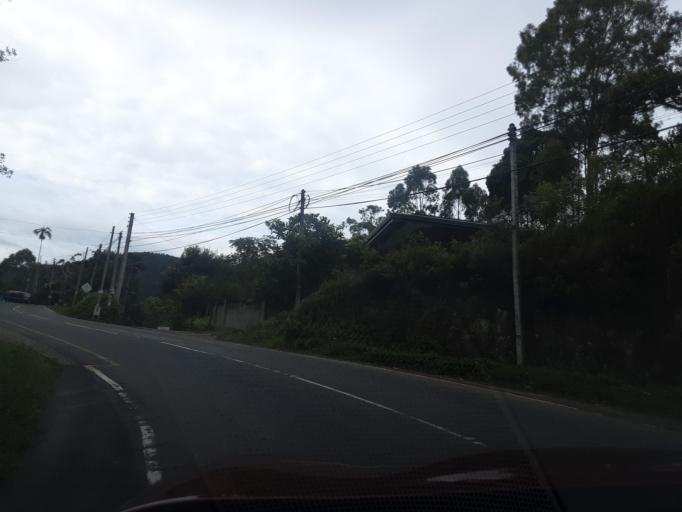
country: LK
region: Uva
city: Haputale
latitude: 6.8510
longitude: 80.9670
